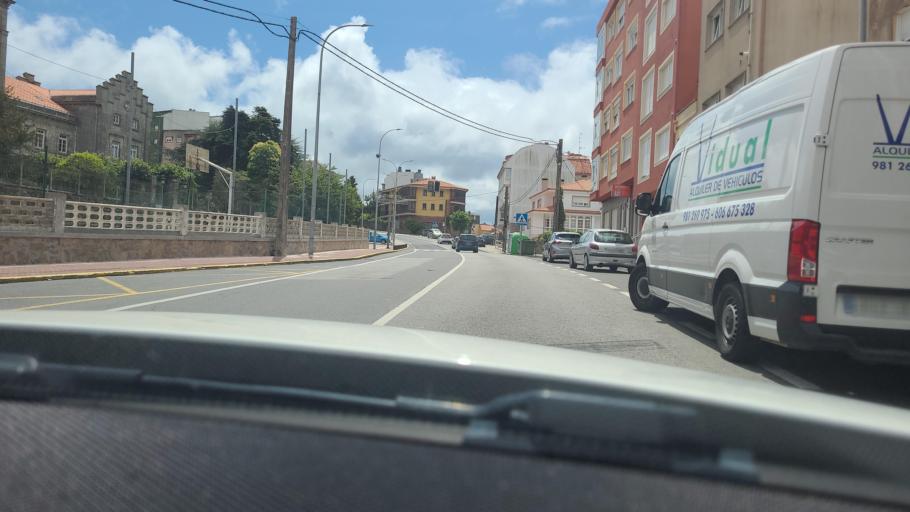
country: ES
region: Galicia
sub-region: Provincia da Coruna
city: Cee
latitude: 42.9556
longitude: -9.1876
